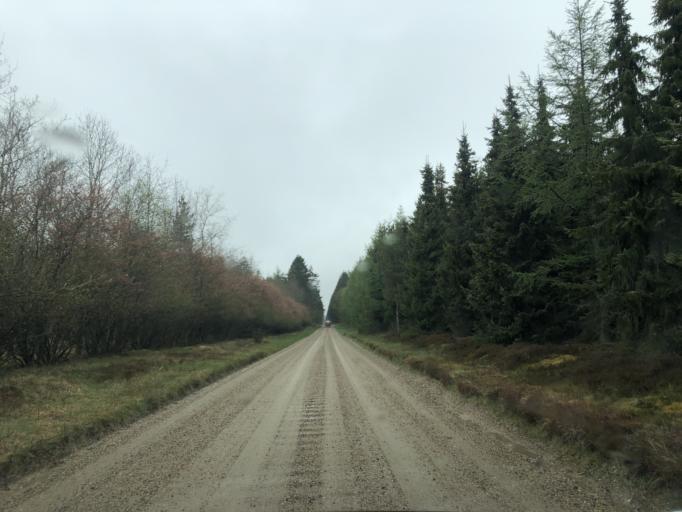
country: DK
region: Central Jutland
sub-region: Lemvig Kommune
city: Lemvig
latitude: 56.4627
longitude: 8.3989
